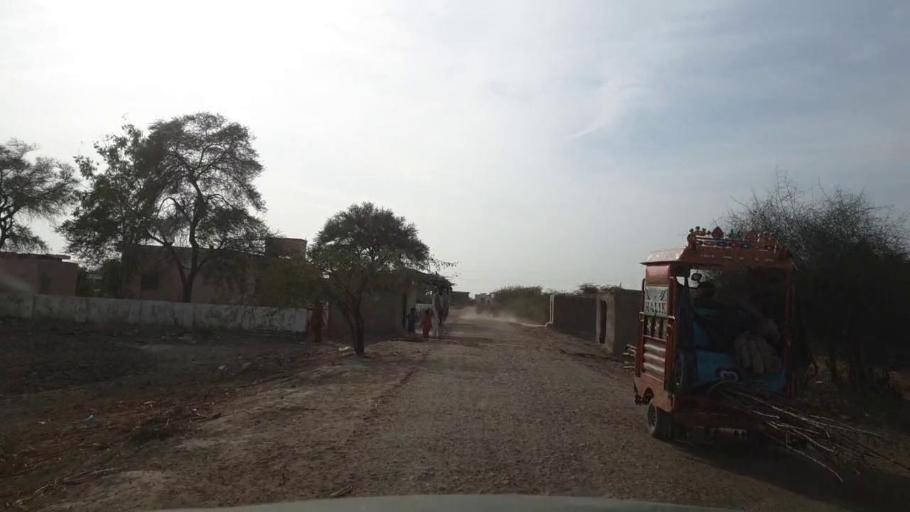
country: PK
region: Sindh
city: Kunri
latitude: 25.1430
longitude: 69.4977
